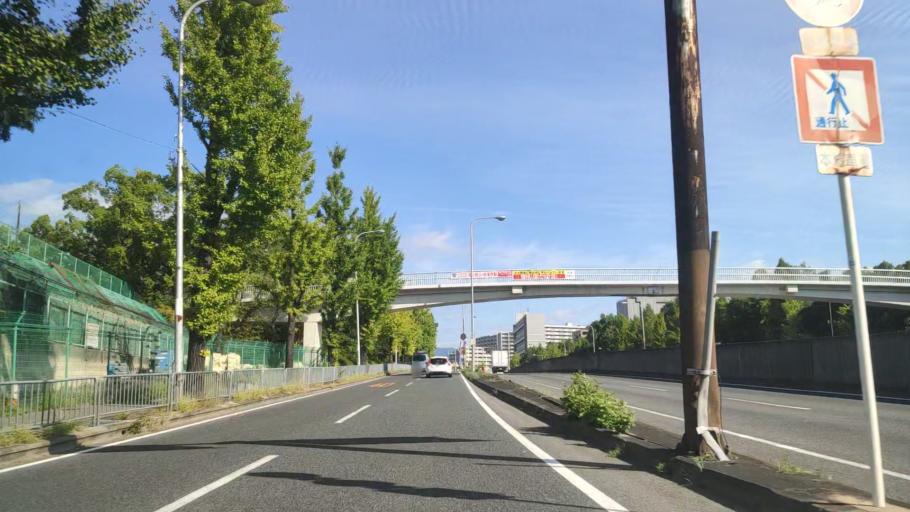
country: JP
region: Osaka
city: Toyonaka
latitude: 34.7895
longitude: 135.4973
